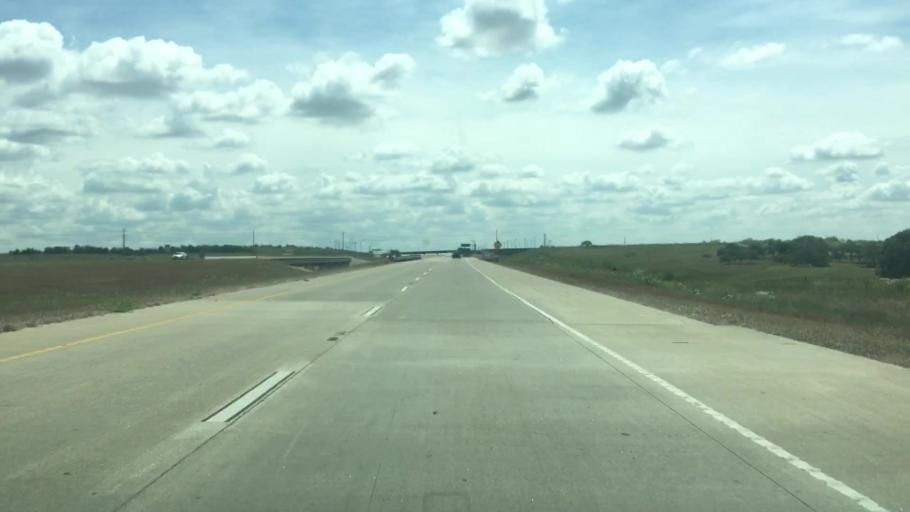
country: US
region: Texas
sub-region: Travis County
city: Onion Creek
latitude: 30.1085
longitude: -97.7925
